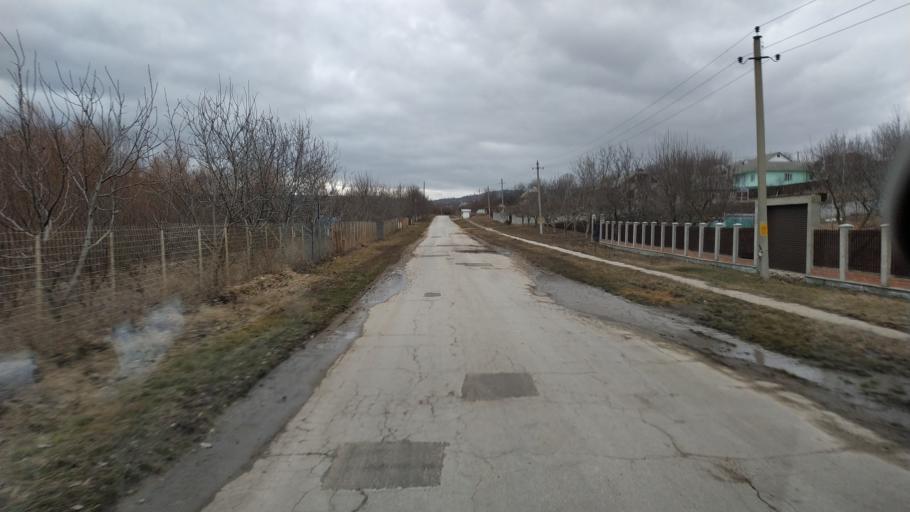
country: MD
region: Calarasi
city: Calarasi
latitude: 47.2515
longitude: 28.1495
